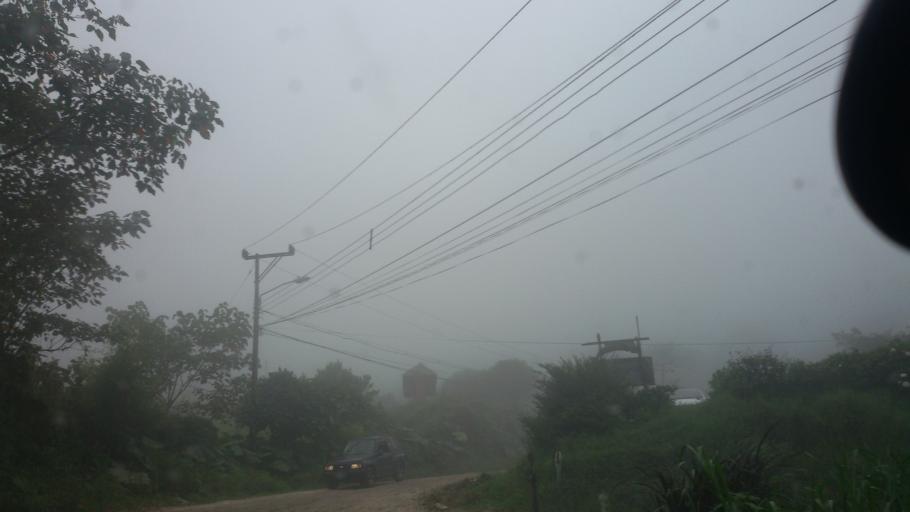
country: CR
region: San Jose
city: Ipis
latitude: 10.0220
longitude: -83.9479
